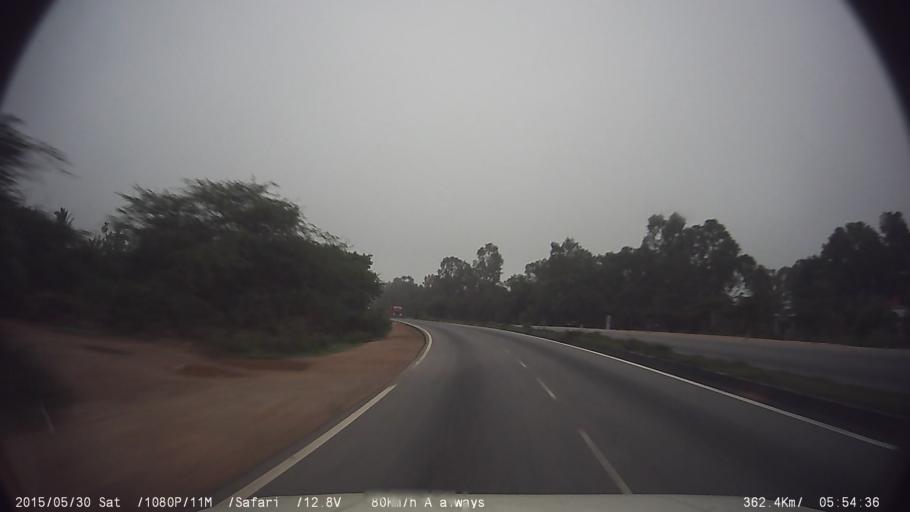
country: IN
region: Karnataka
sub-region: Mandya
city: Shrirangapattana
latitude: 12.4633
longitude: 76.7468
